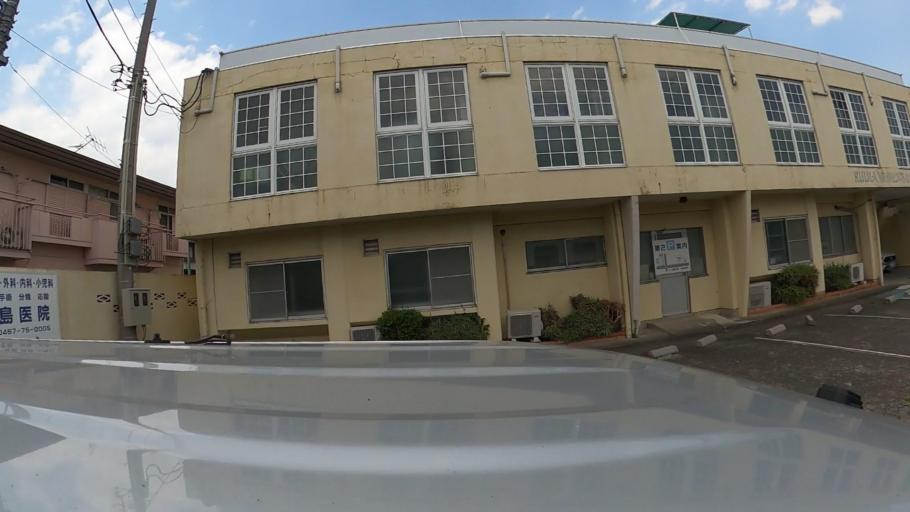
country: JP
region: Kanagawa
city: Chigasaki
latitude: 35.3638
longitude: 139.3838
